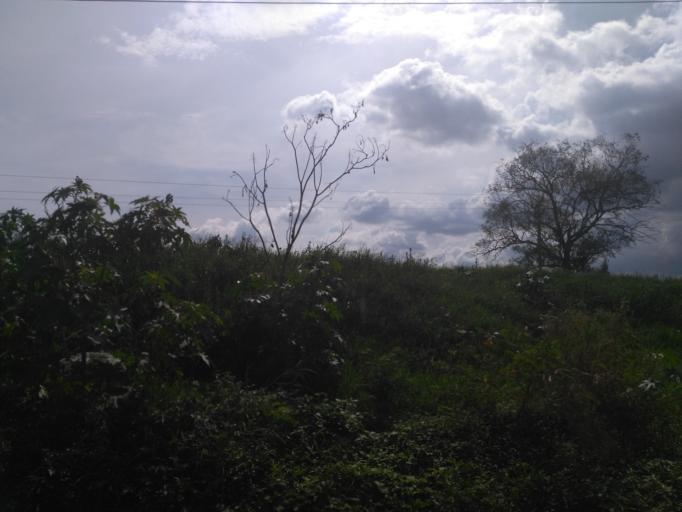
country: UG
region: Eastern Region
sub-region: Jinja District
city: Jinja
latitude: 0.4253
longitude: 33.2205
